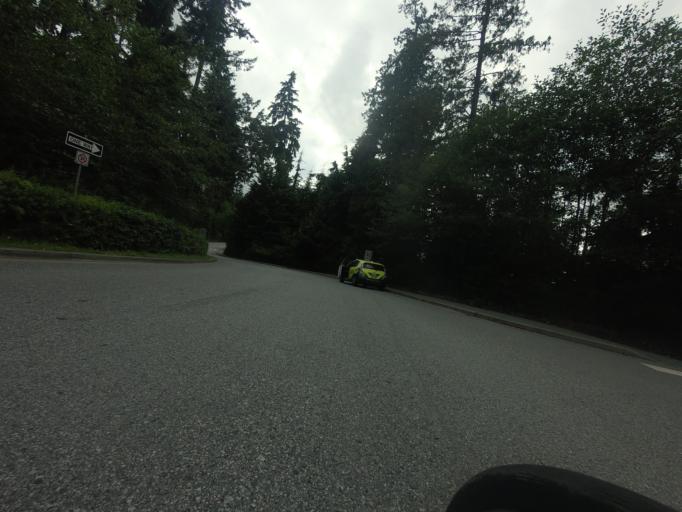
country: CA
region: British Columbia
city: West End
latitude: 49.3125
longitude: -123.1443
